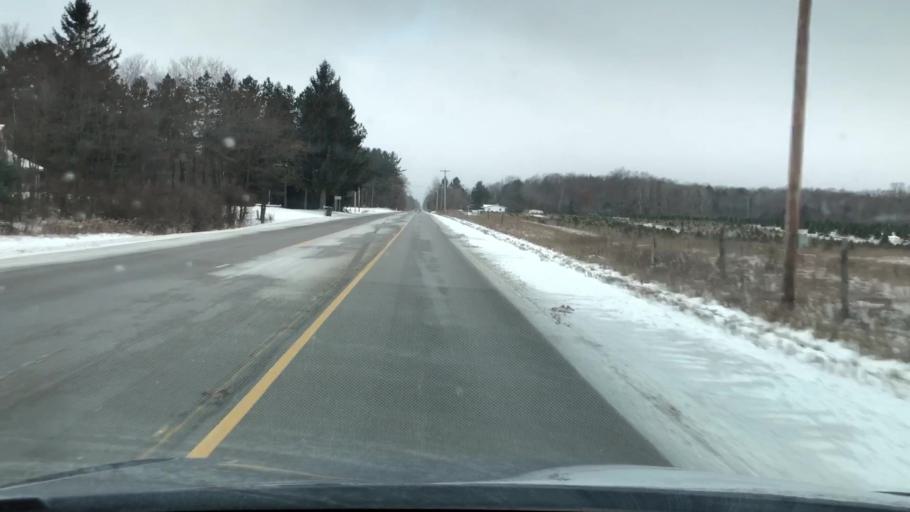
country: US
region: Michigan
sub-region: Wexford County
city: Cadillac
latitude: 44.2812
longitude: -85.4586
